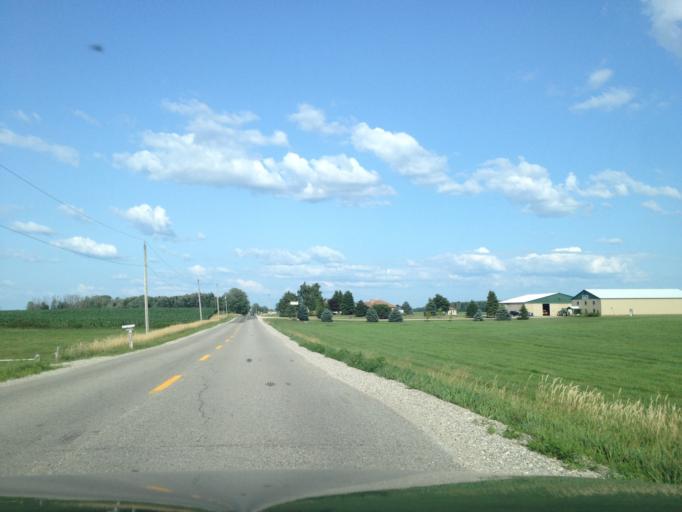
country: CA
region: Ontario
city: Ingersoll
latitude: 42.9621
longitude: -80.7684
